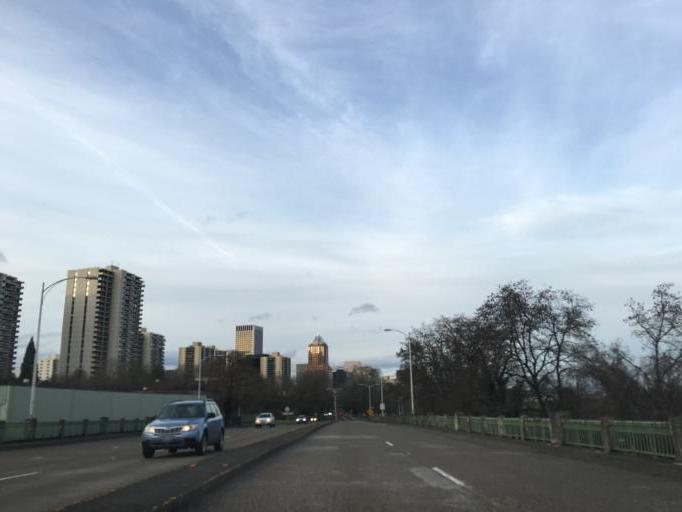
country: US
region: Oregon
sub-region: Multnomah County
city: Portland
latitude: 45.5037
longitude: -122.6777
